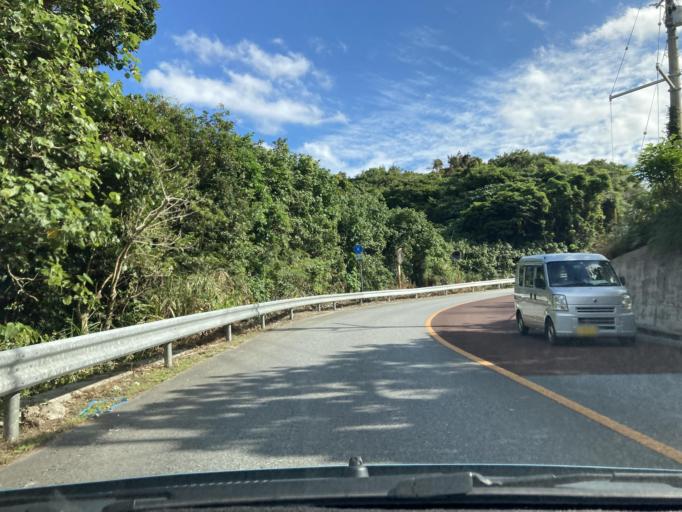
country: JP
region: Okinawa
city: Ishikawa
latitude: 26.4382
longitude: 127.8052
